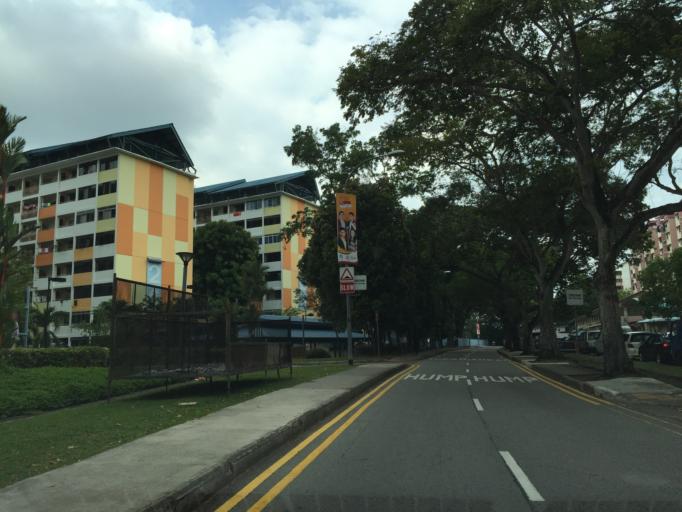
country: SG
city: Singapore
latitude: 1.2987
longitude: 103.7991
